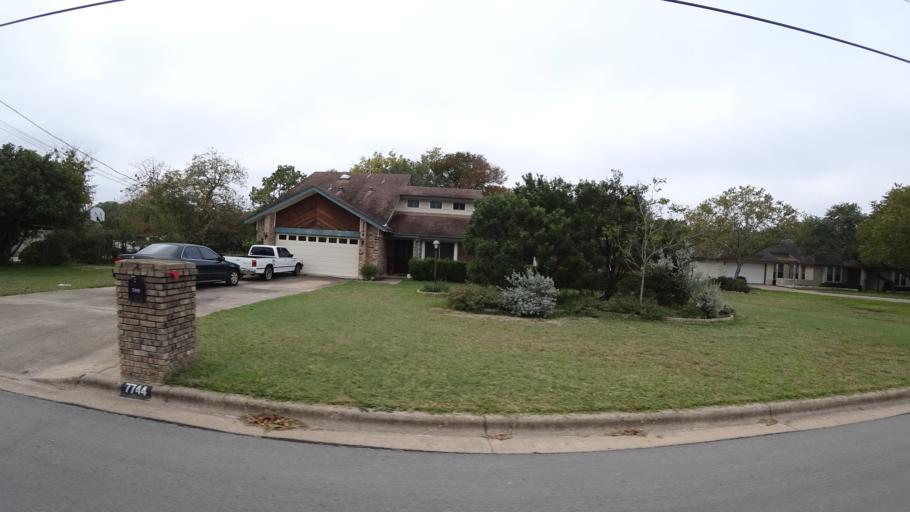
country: US
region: Texas
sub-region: Travis County
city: Shady Hollow
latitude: 30.2167
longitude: -97.9111
